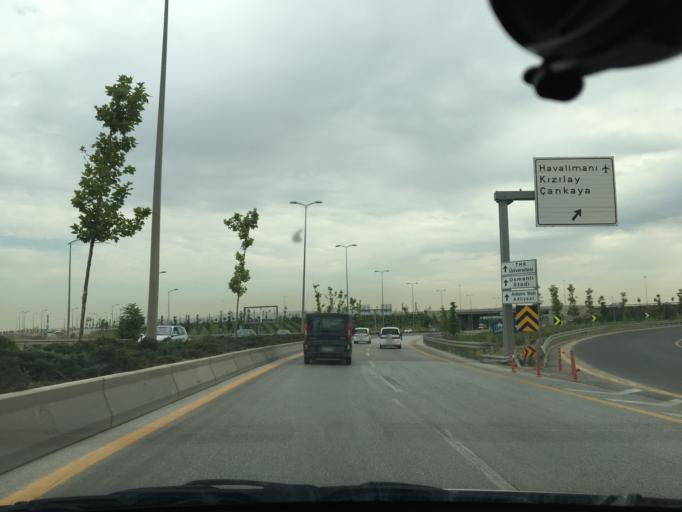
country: TR
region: Ankara
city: Batikent
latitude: 39.9227
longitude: 32.7059
